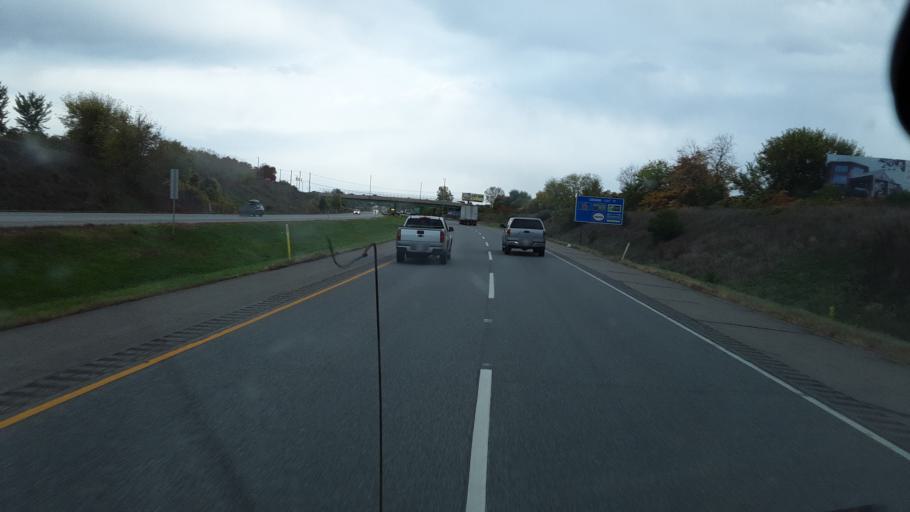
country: US
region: Indiana
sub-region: Saint Joseph County
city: South Bend
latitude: 41.7220
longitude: -86.2899
